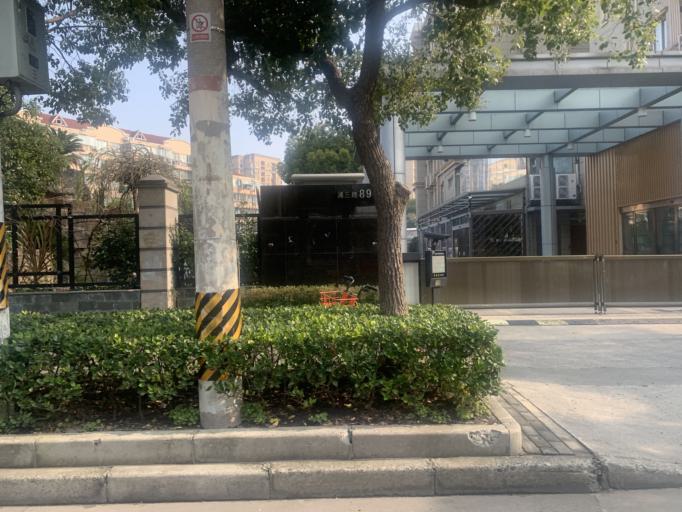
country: CN
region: Shanghai Shi
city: Huamu
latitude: 31.1831
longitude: 121.5155
